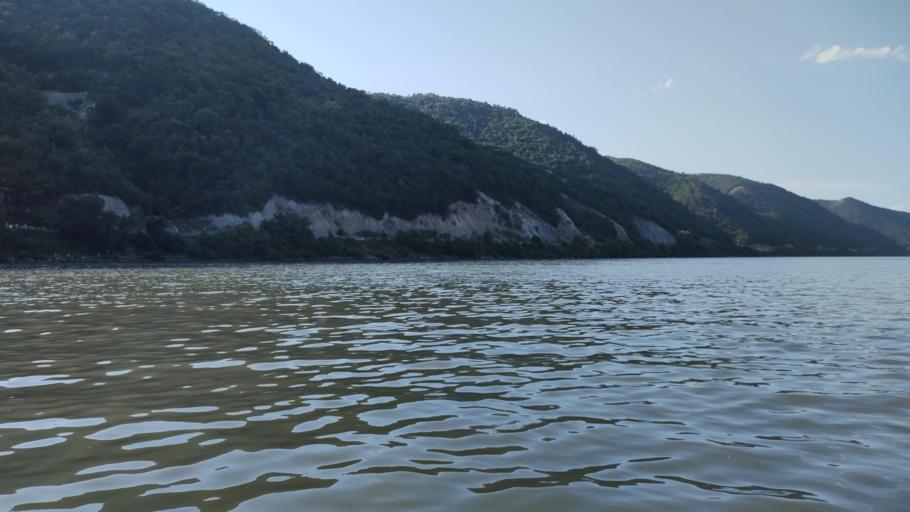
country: RO
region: Mehedinti
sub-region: Comuna Svinita
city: Svinita
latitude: 44.4918
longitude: 22.1862
